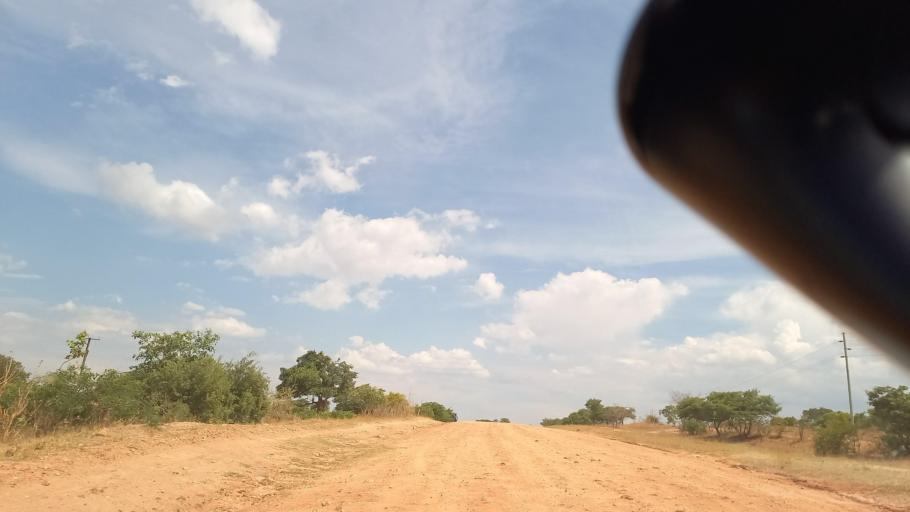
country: ZM
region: Lusaka
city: Kafue
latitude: -16.1304
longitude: 28.0473
